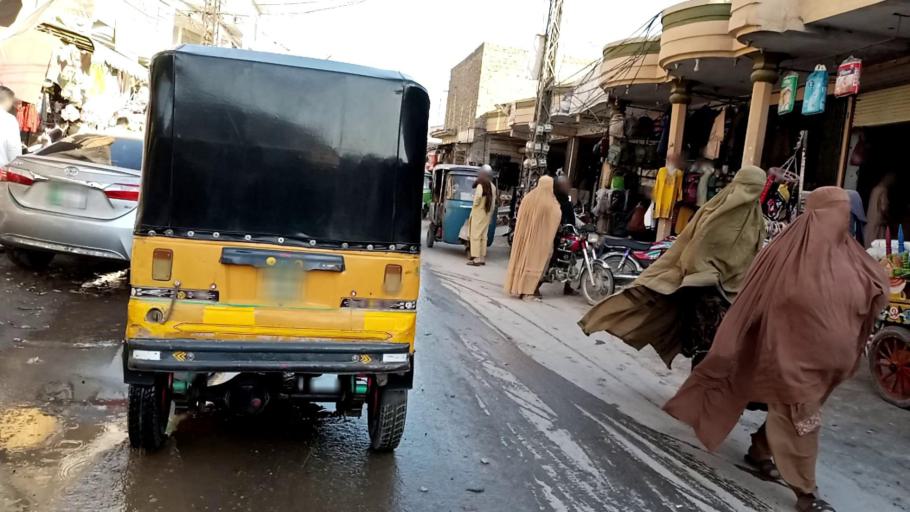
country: PK
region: Khyber Pakhtunkhwa
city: Peshawar
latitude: 34.0562
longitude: 71.5405
